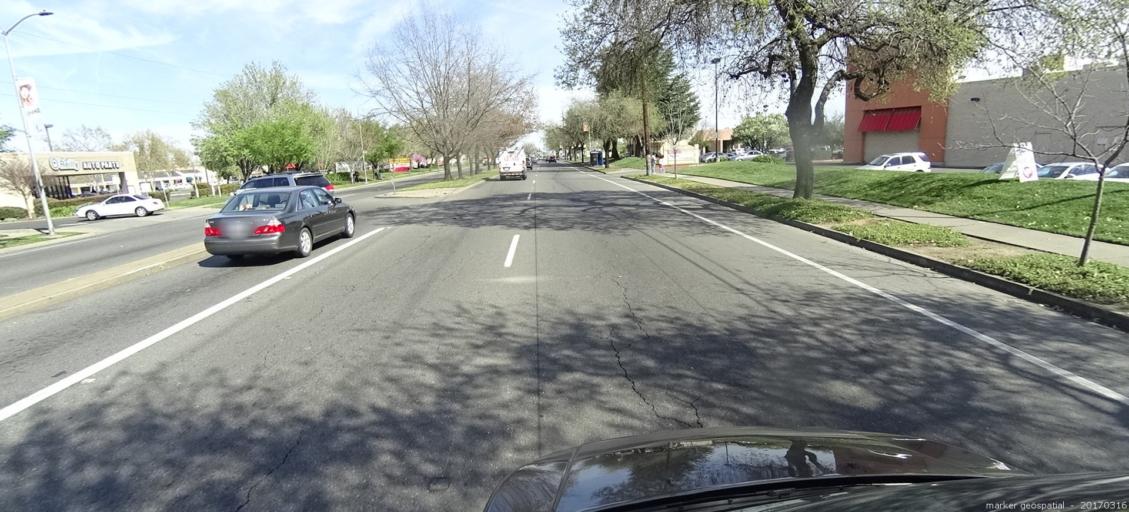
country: US
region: California
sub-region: Sacramento County
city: Florin
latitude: 38.4742
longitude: -121.4319
